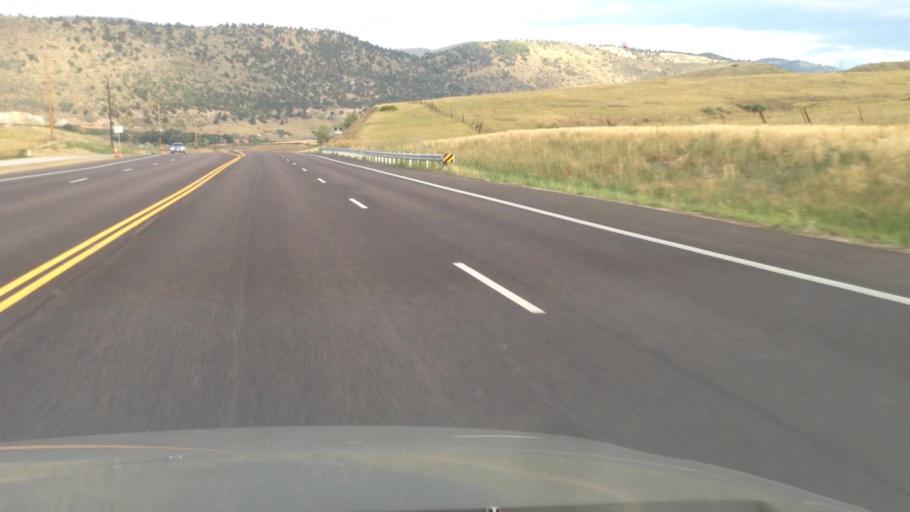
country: US
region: Colorado
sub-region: Jefferson County
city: West Pleasant View
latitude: 39.6829
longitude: -105.1774
